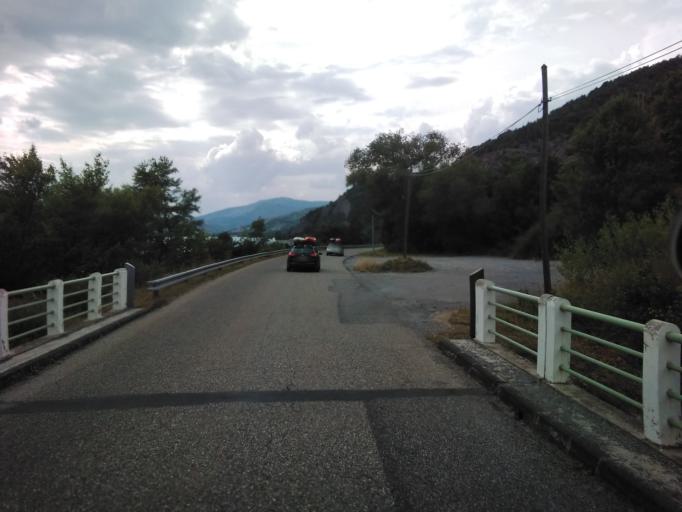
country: FR
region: Provence-Alpes-Cote d'Azur
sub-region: Departement des Alpes-de-Haute-Provence
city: Seyne-les-Alpes
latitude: 44.4600
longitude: 6.3752
